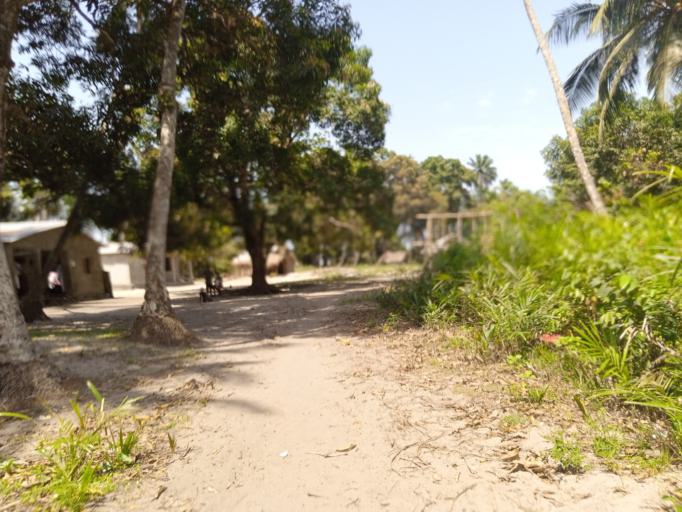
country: SL
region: Western Area
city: Waterloo
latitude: 8.2651
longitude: -13.0005
